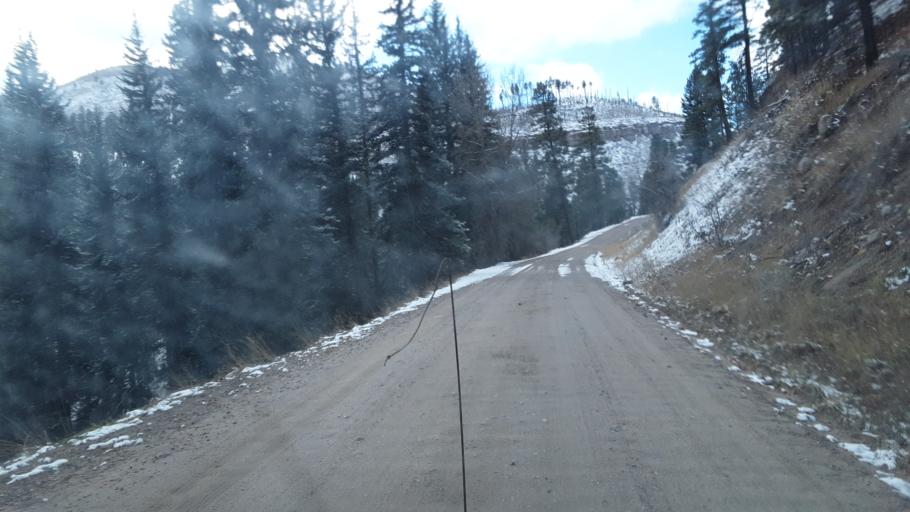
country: US
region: Colorado
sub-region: La Plata County
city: Bayfield
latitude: 37.4114
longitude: -107.5172
